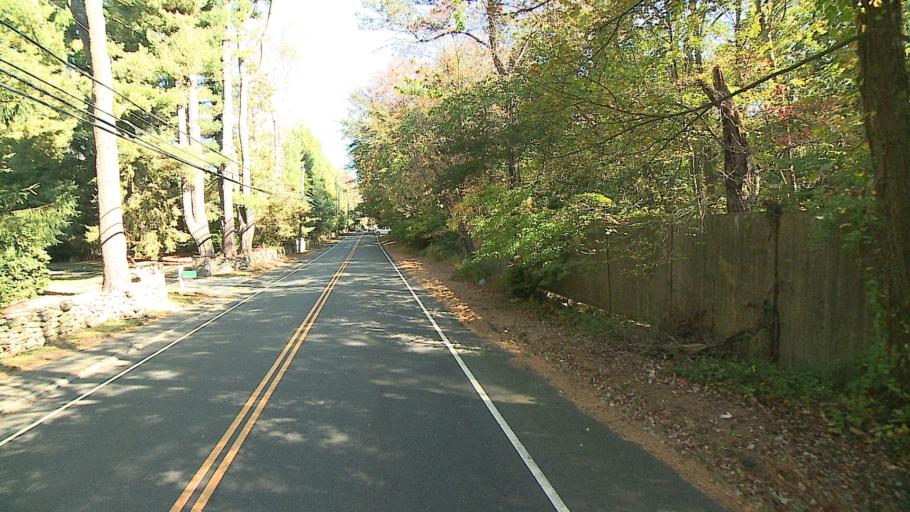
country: US
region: Connecticut
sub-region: Fairfield County
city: Westport
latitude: 41.1797
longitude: -73.3458
